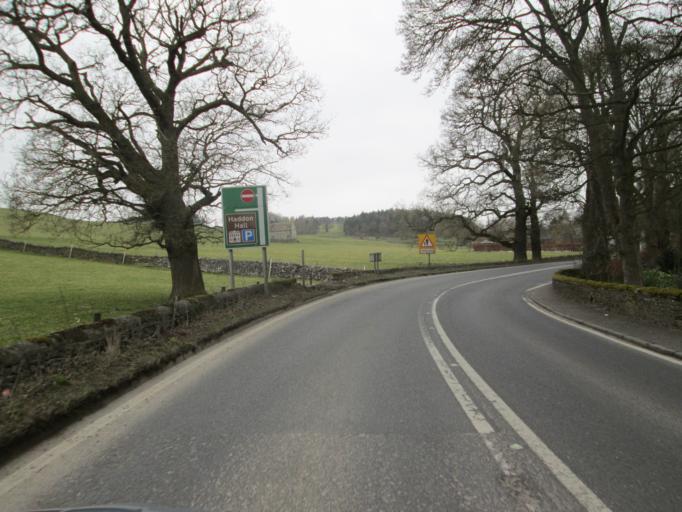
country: GB
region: England
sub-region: Derbyshire
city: Bakewell
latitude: 53.1905
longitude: -1.6495
